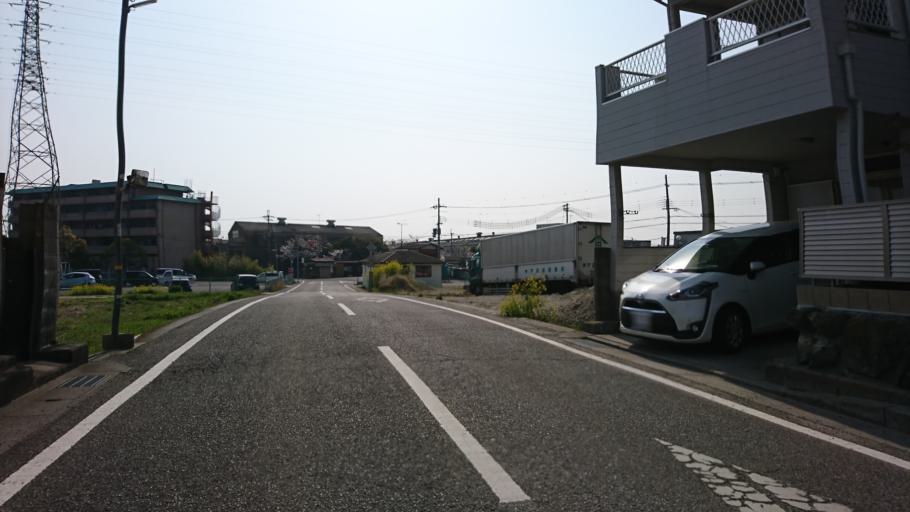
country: JP
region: Hyogo
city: Kakogawacho-honmachi
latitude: 34.7327
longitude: 134.8910
